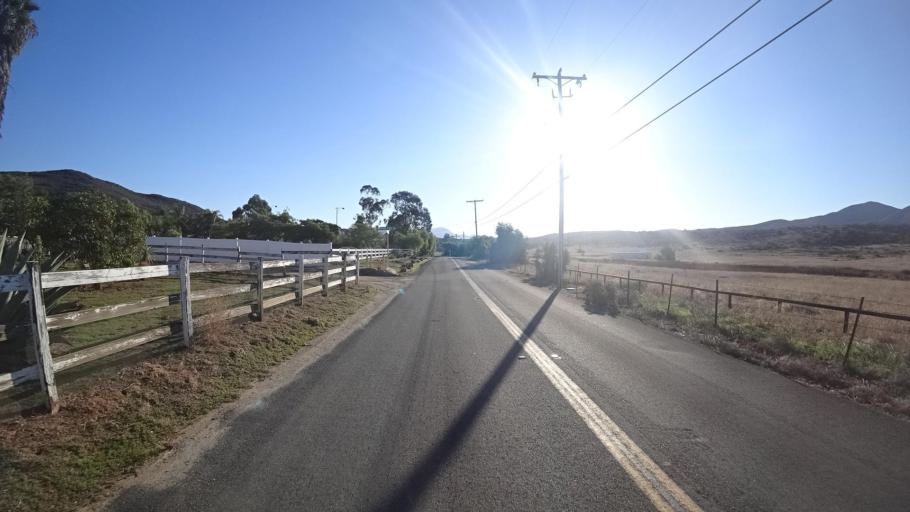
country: US
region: California
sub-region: San Diego County
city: Jamul
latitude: 32.7028
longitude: -116.9002
